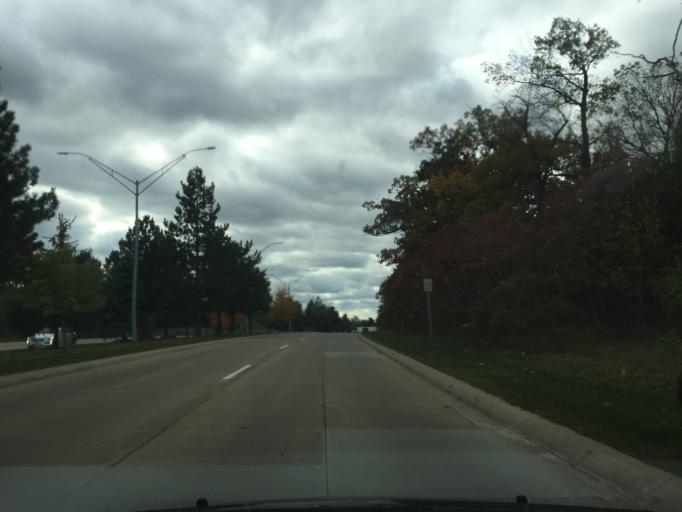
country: US
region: Michigan
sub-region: Oakland County
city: Auburn Hills
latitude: 42.6572
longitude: -83.2179
